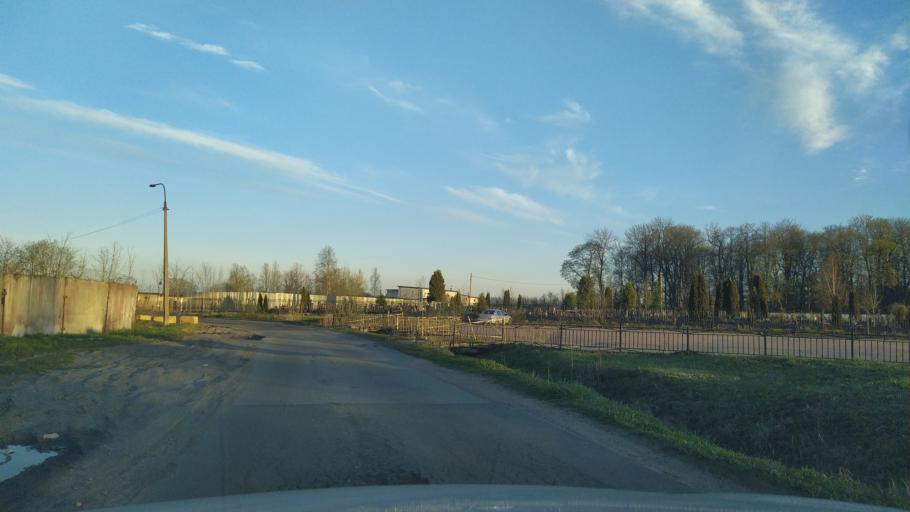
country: RU
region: St.-Petersburg
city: Pushkin
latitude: 59.6955
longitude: 30.3899
